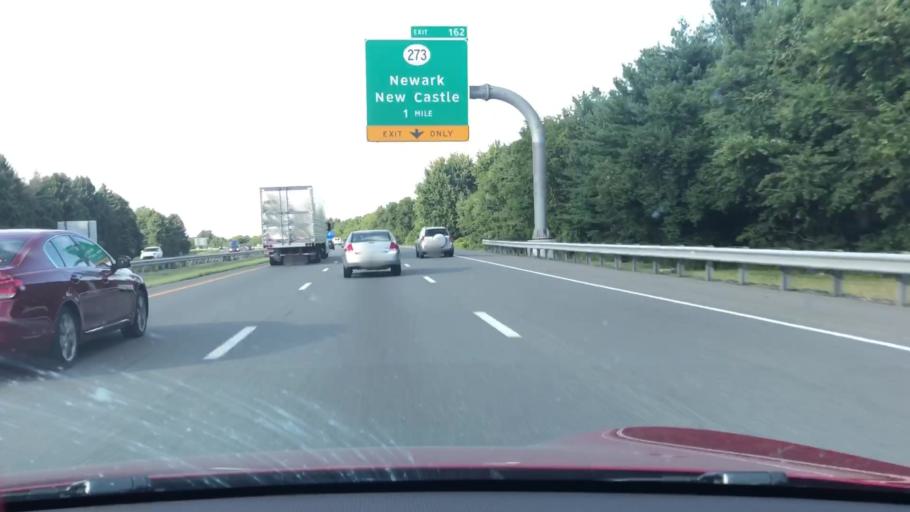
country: US
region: Delaware
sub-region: New Castle County
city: Bear
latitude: 39.6423
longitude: -75.6511
